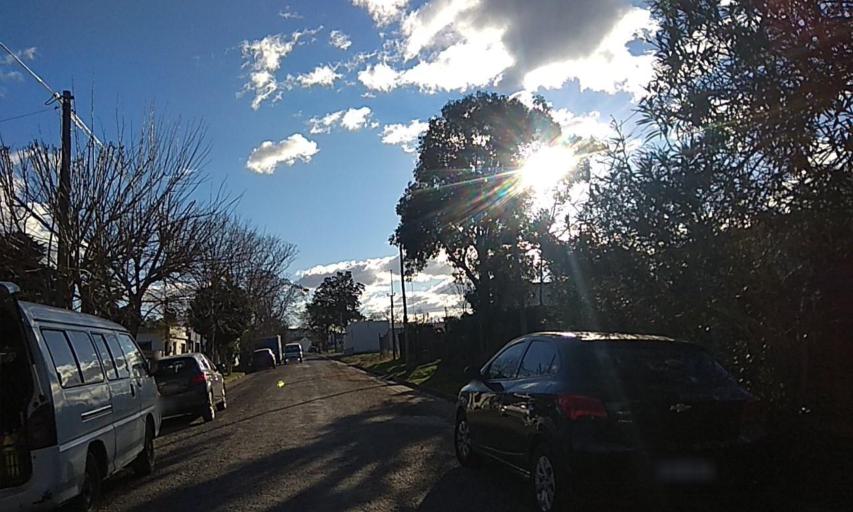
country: UY
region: Florida
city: Florida
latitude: -34.0994
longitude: -56.2289
